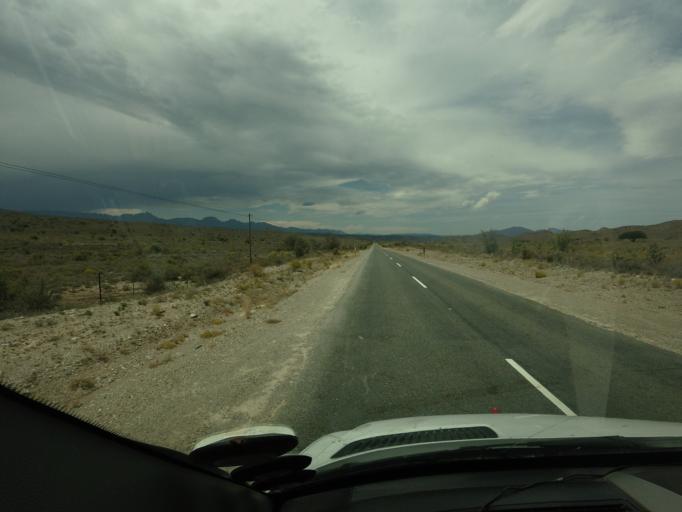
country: ZA
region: Western Cape
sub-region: Eden District Municipality
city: Ladismith
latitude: -33.6037
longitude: 21.0794
